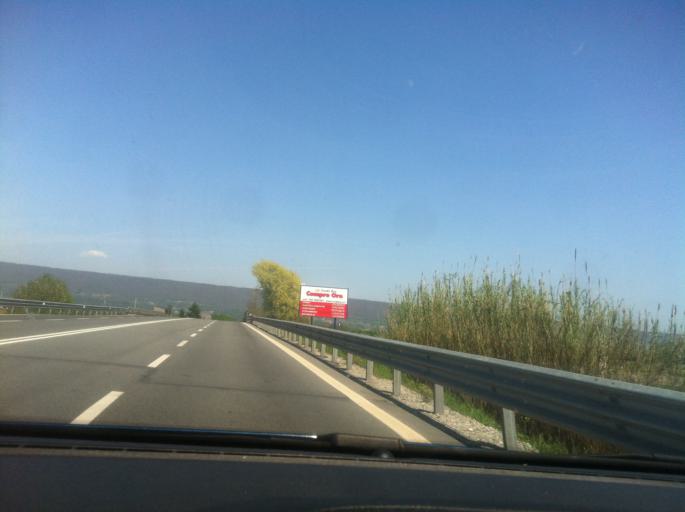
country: IT
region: Piedmont
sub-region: Provincia di Torino
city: Ivrea
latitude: 45.4436
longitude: 7.8848
